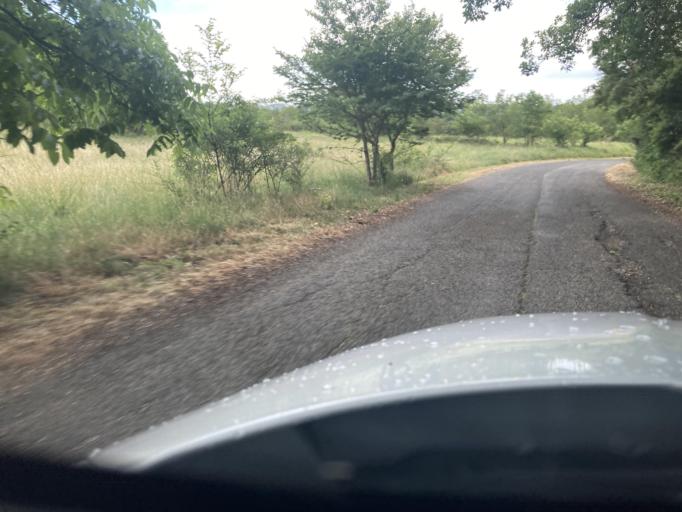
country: IT
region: Abruzzo
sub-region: Provincia dell' Aquila
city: Fossa
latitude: 42.2830
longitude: 13.4853
